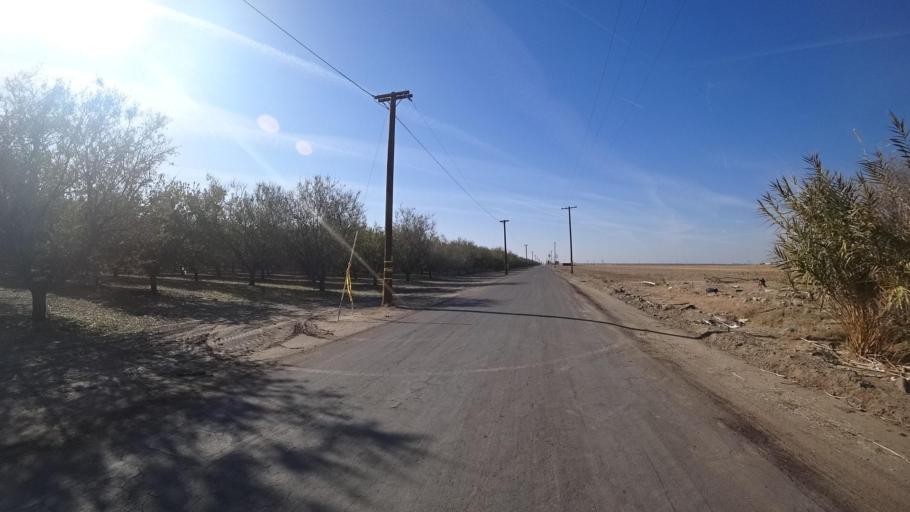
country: US
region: California
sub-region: Kern County
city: Wasco
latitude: 35.6598
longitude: -119.3842
